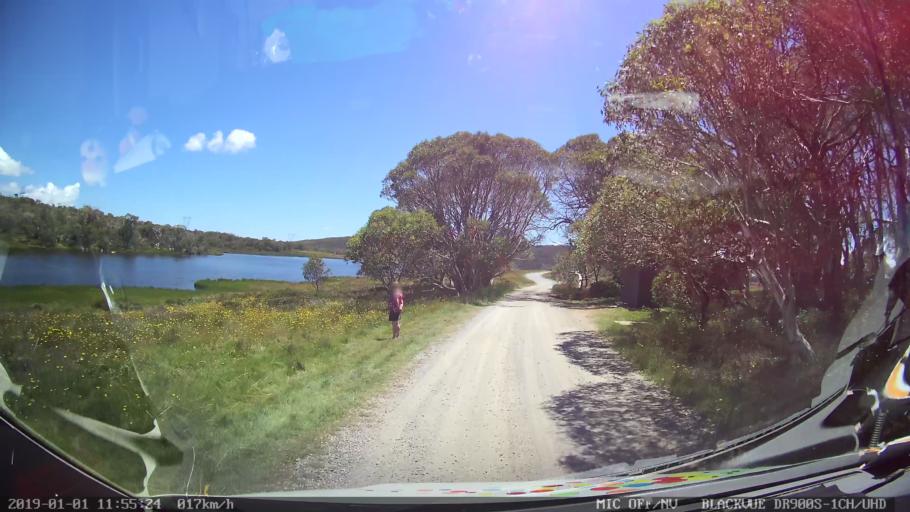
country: AU
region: New South Wales
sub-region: Snowy River
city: Jindabyne
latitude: -35.8884
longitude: 148.4485
